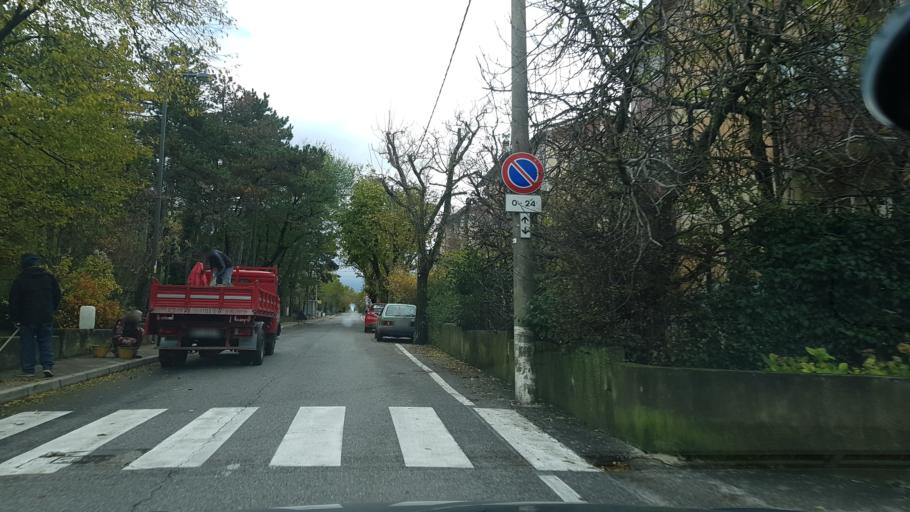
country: IT
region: Friuli Venezia Giulia
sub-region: Provincia di Trieste
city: Prosecco-Contovello
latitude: 45.7010
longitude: 13.7390
